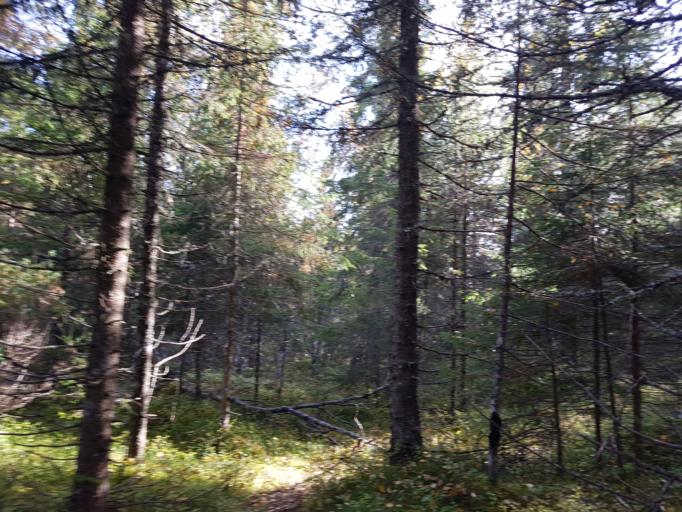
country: NO
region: Sor-Trondelag
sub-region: Trondheim
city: Trondheim
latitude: 63.4482
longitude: 10.2807
